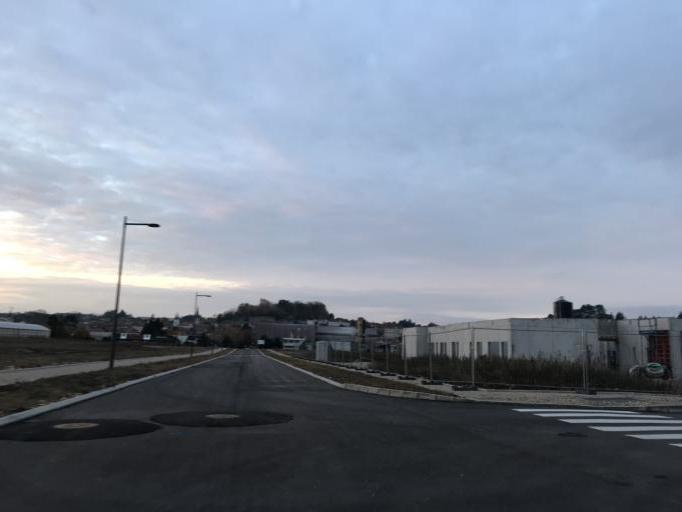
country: FR
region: Rhone-Alpes
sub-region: Departement de l'Ain
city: Meximieux
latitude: 45.8986
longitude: 5.1994
